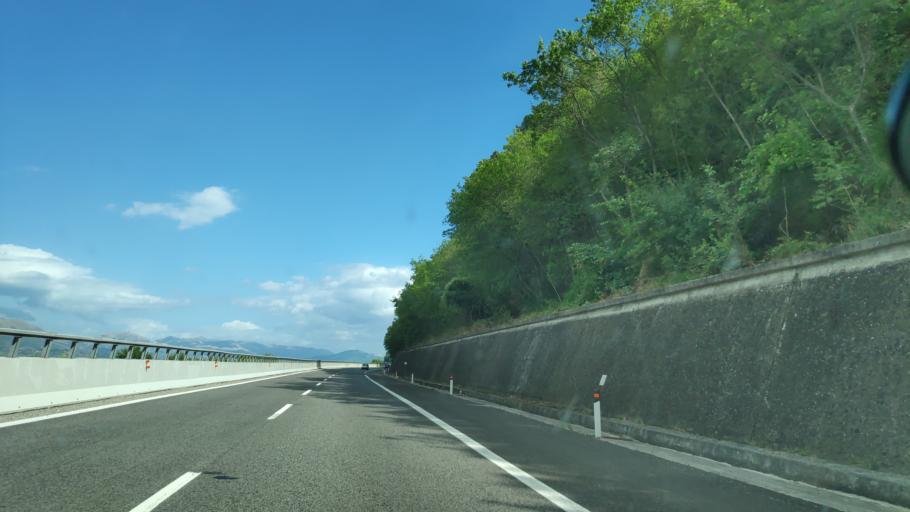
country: IT
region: Campania
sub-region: Provincia di Salerno
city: Sicignano degli Alburni
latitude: 40.5968
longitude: 15.3188
